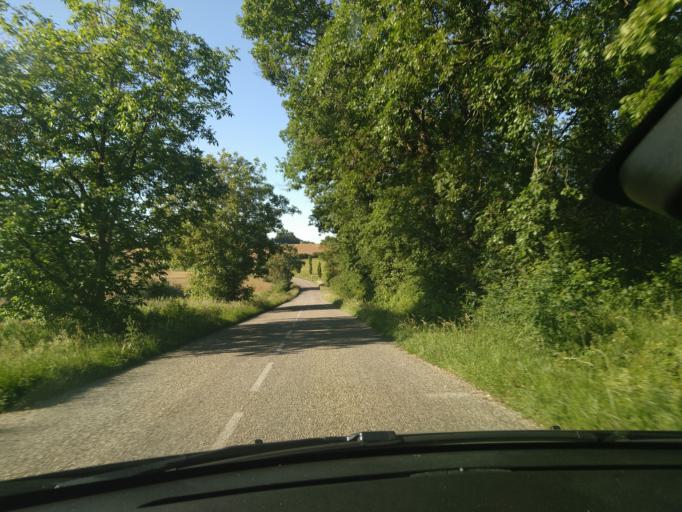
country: FR
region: Midi-Pyrenees
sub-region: Departement du Gers
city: Gimont
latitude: 43.6954
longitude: 0.8765
